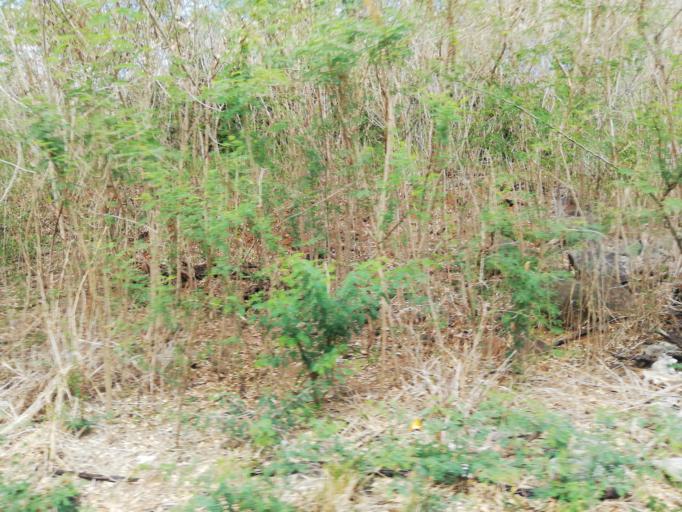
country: MU
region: Moka
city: Pailles
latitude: -20.1930
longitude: 57.4732
